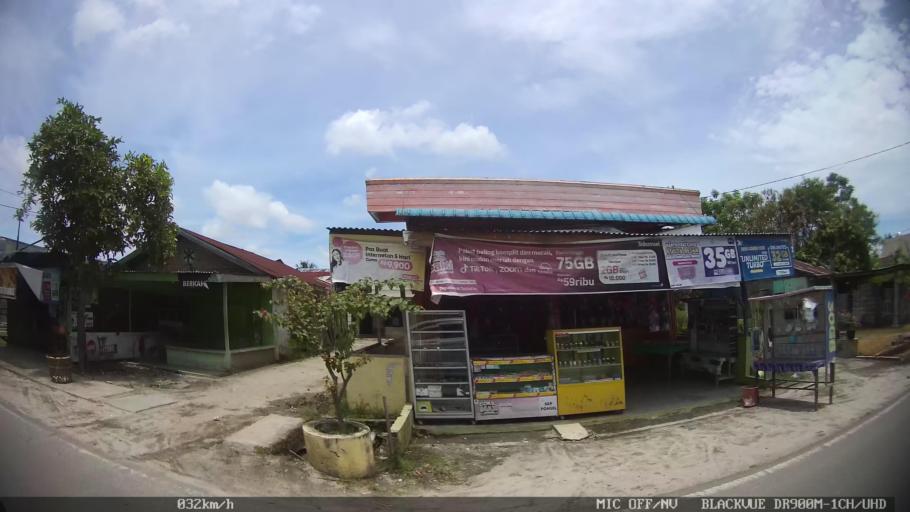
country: ID
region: North Sumatra
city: Percut
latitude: 3.5677
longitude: 98.8831
